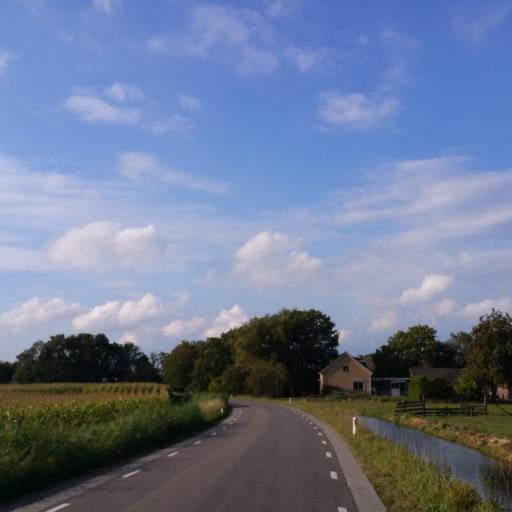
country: NL
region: Utrecht
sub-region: Gemeente IJsselstein
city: IJsselstein
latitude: 52.0465
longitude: 5.0095
